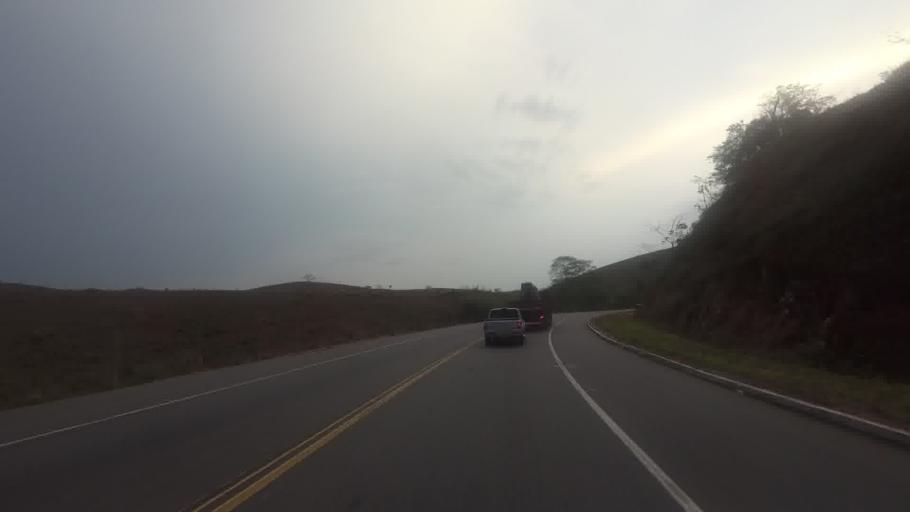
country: BR
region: Rio de Janeiro
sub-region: Carmo
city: Carmo
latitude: -21.8126
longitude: -42.5941
